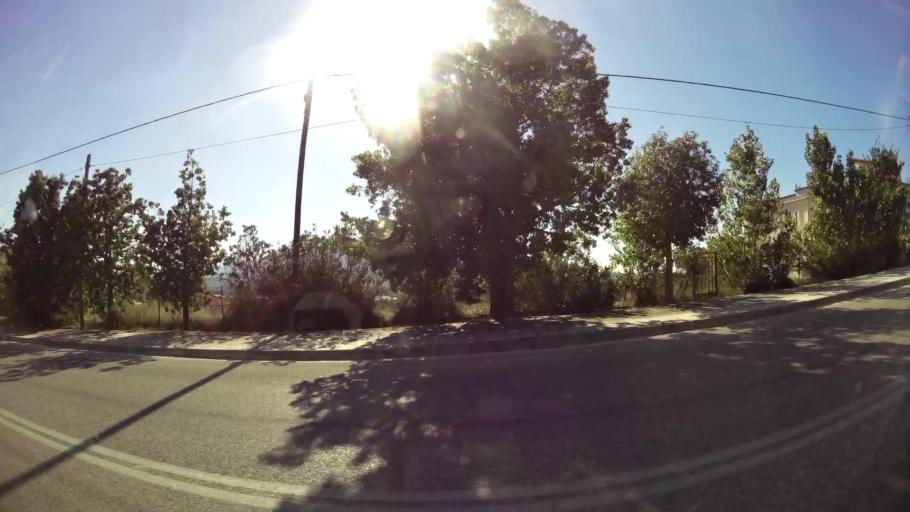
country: GR
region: Attica
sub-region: Nomarchia Anatolikis Attikis
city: Anthousa
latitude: 38.0202
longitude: 23.8720
